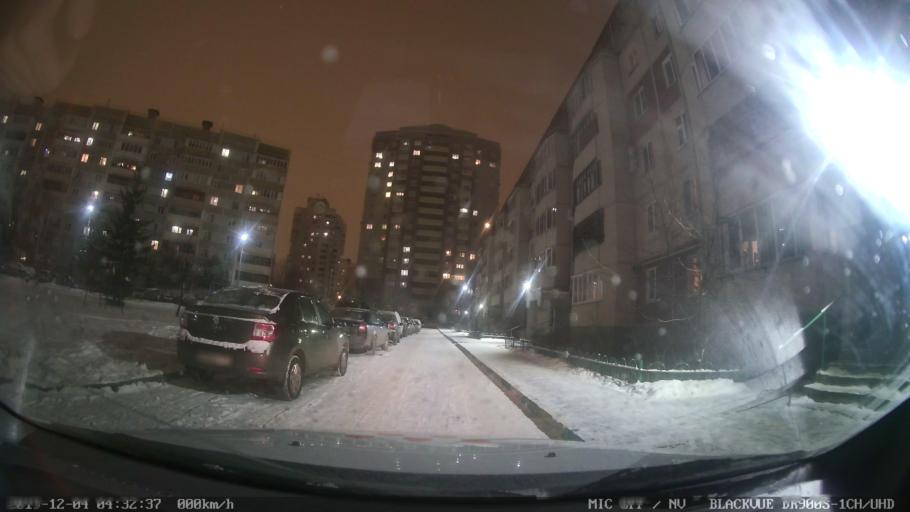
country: RU
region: Tatarstan
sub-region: Gorod Kazan'
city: Kazan
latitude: 55.7421
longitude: 49.1993
